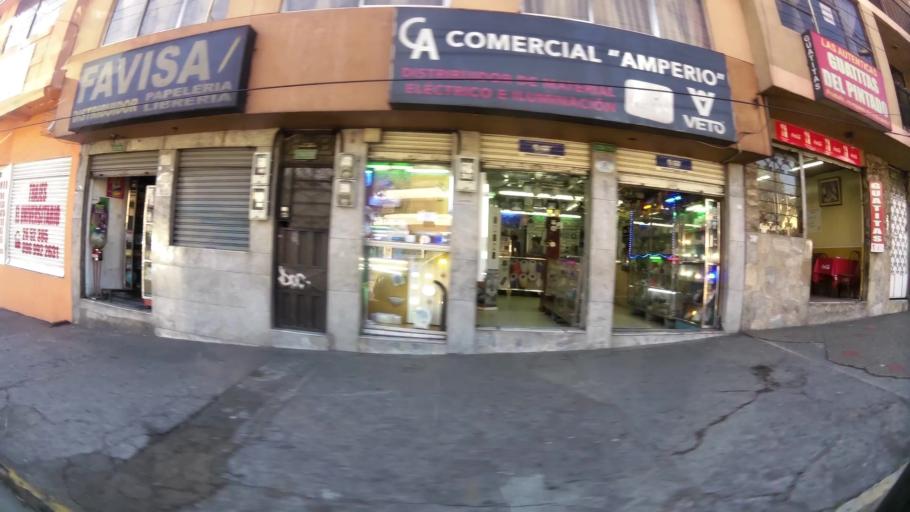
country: EC
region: Pichincha
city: Quito
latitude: -0.2466
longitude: -78.5344
